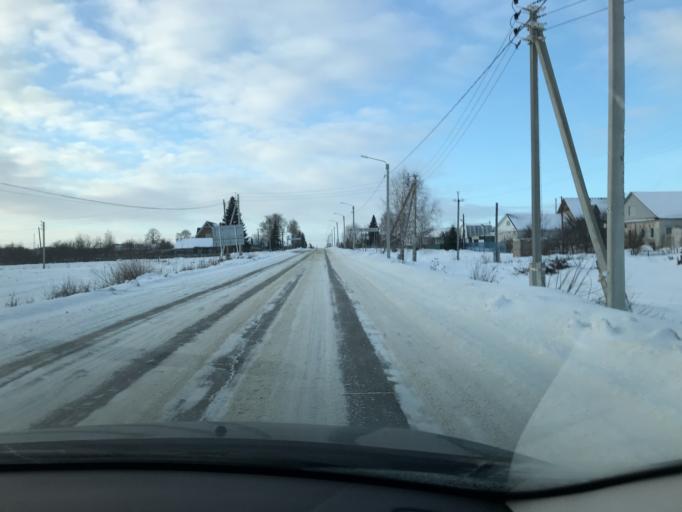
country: RU
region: Ulyanovsk
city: Undory
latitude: 54.6030
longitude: 48.4150
